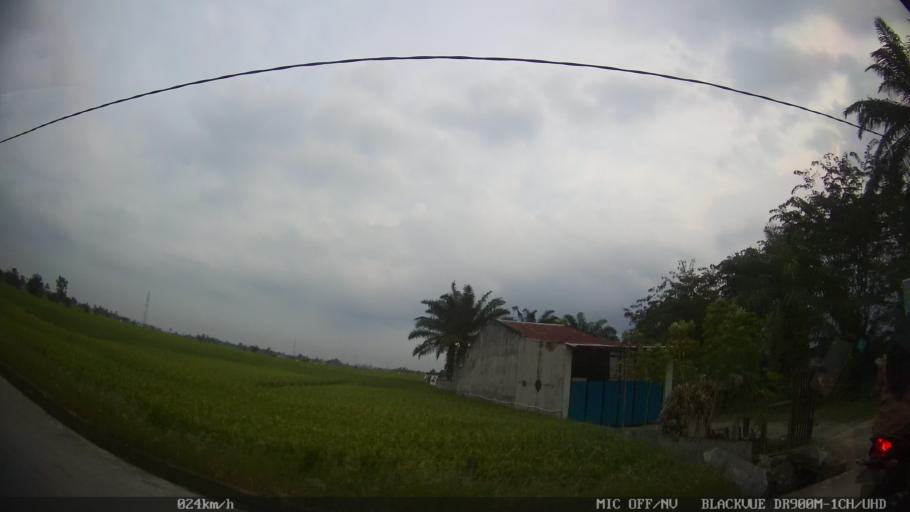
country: ID
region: North Sumatra
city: Sunggal
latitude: 3.5610
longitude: 98.5887
